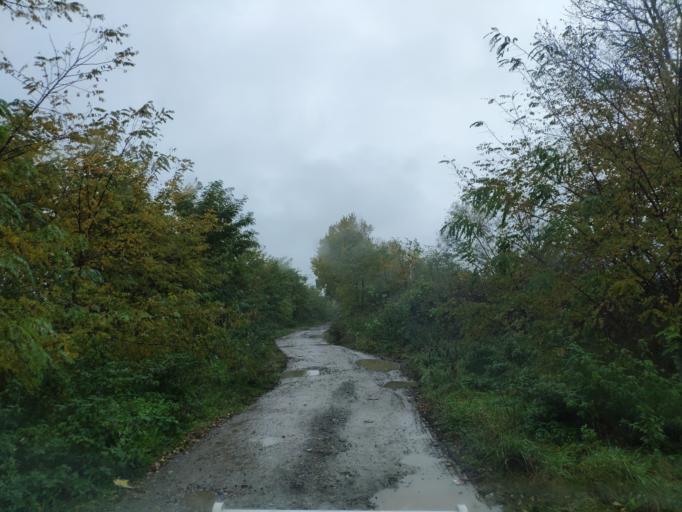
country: SK
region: Kosicky
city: Cierna nad Tisou
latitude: 48.4471
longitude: 21.9970
